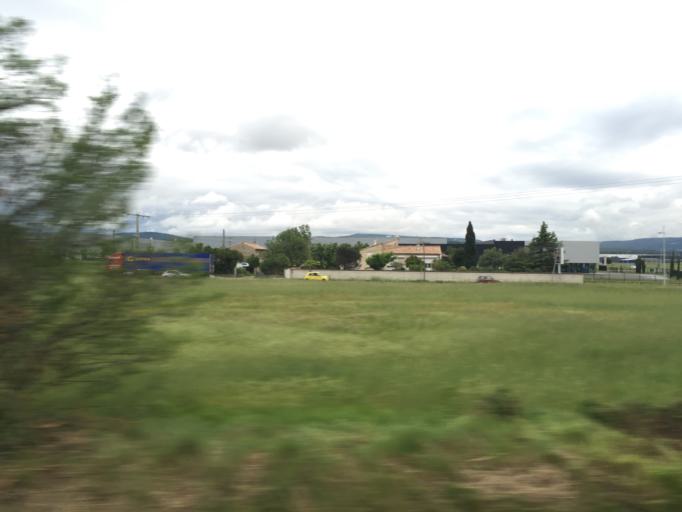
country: FR
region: Rhone-Alpes
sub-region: Departement de la Drome
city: Montelimar
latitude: 44.5289
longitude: 4.7341
